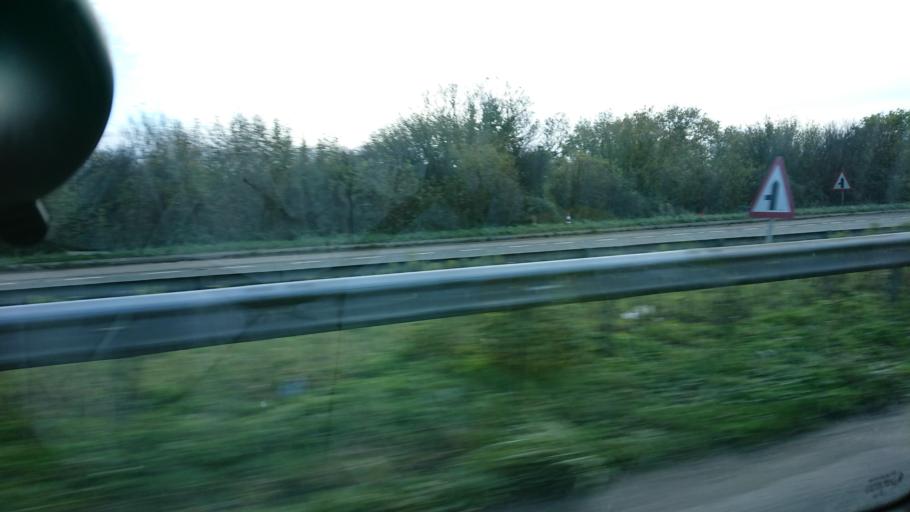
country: GB
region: England
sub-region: Devon
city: Yealmpton
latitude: 50.3814
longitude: -3.9995
